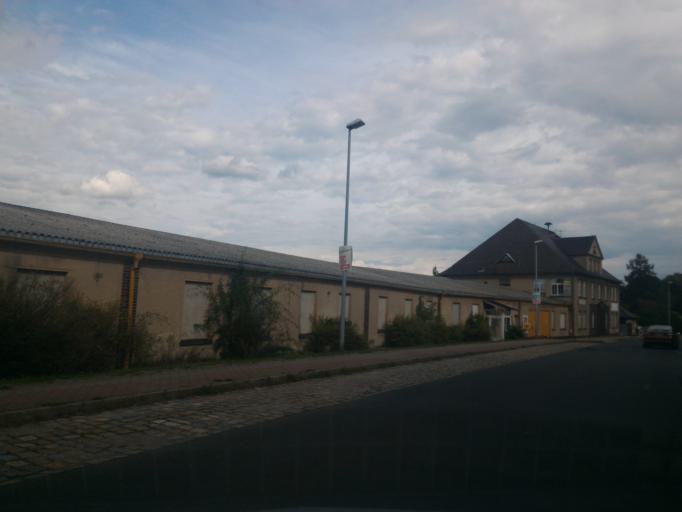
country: DE
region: Saxony
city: Krauschwitz
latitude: 51.5229
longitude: 14.7026
